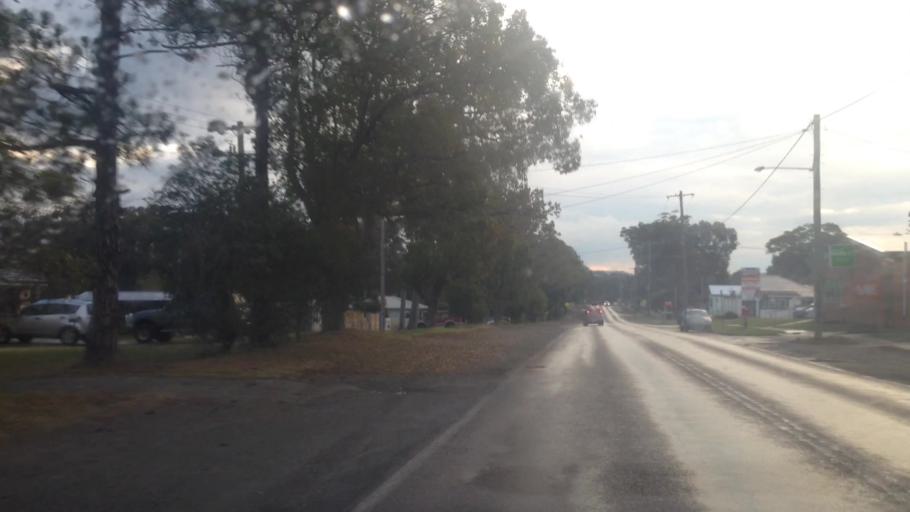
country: AU
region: New South Wales
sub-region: Wyong Shire
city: Charmhaven
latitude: -33.1758
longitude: 151.4861
